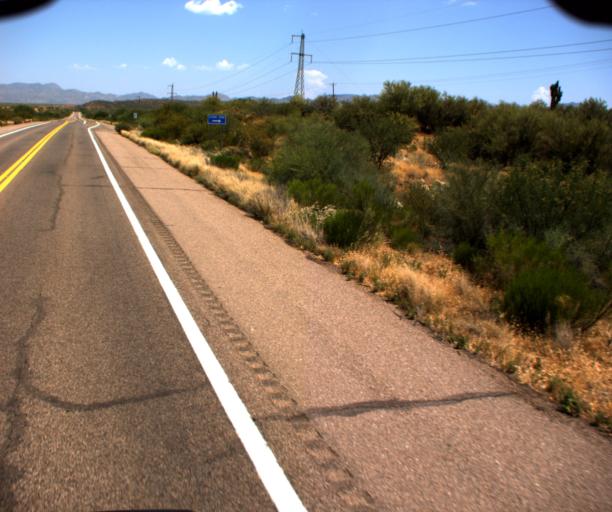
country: US
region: Arizona
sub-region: Gila County
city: Tonto Basin
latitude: 33.6445
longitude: -111.0893
